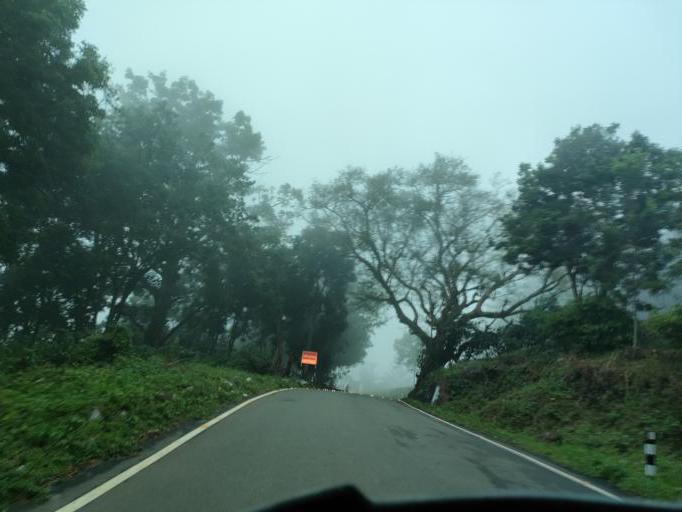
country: IN
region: Tamil Nadu
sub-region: Dindigul
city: Ayakudi
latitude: 10.3562
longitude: 77.5641
